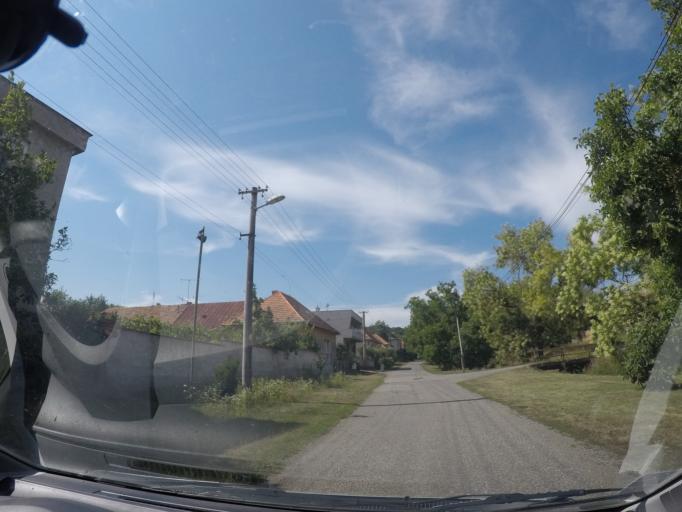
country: SK
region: Banskobystricky
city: Nova Bana
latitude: 48.3279
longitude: 18.7077
